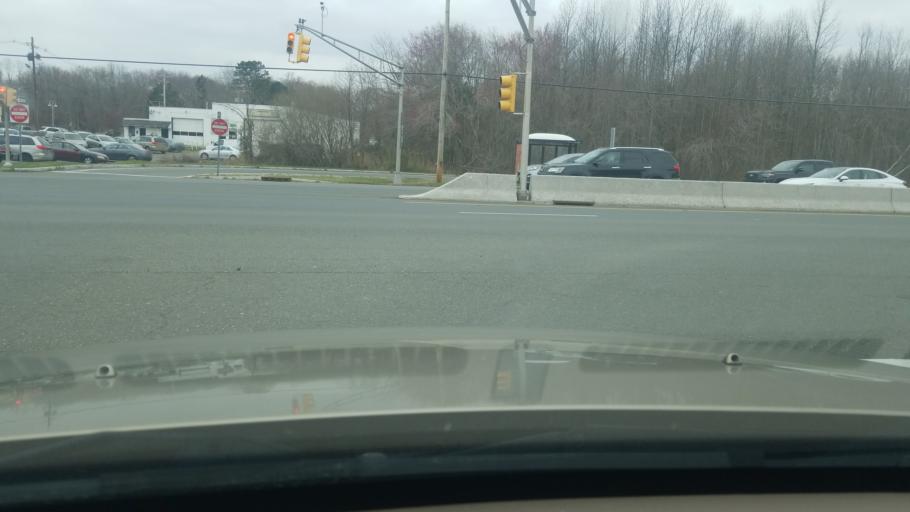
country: US
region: New Jersey
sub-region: Ocean County
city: Lakewood
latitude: 40.1154
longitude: -74.2186
